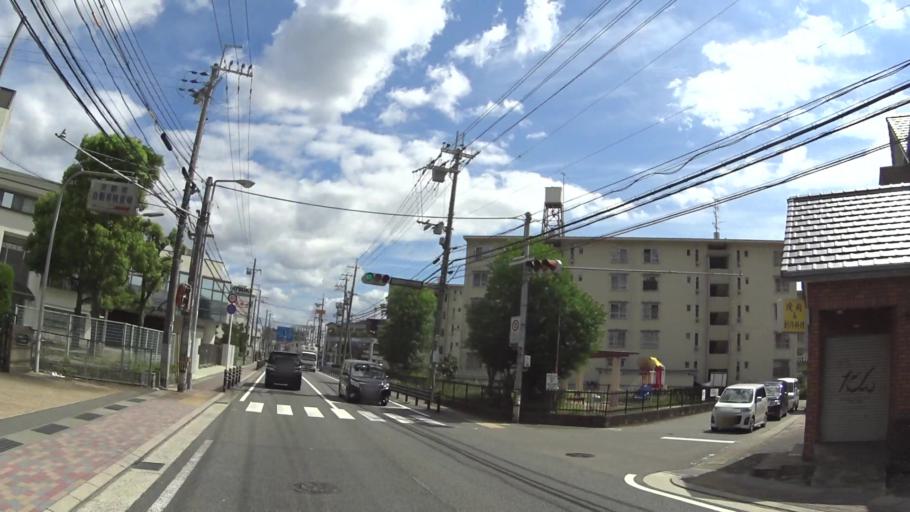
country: JP
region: Kyoto
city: Yawata
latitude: 34.8773
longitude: 135.7421
